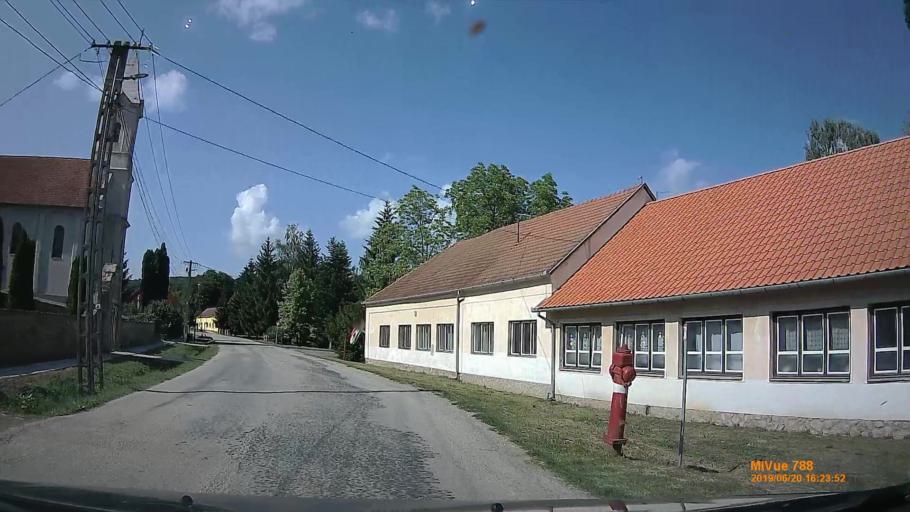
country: HU
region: Baranya
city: Buekkoesd
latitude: 46.1314
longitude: 18.0441
